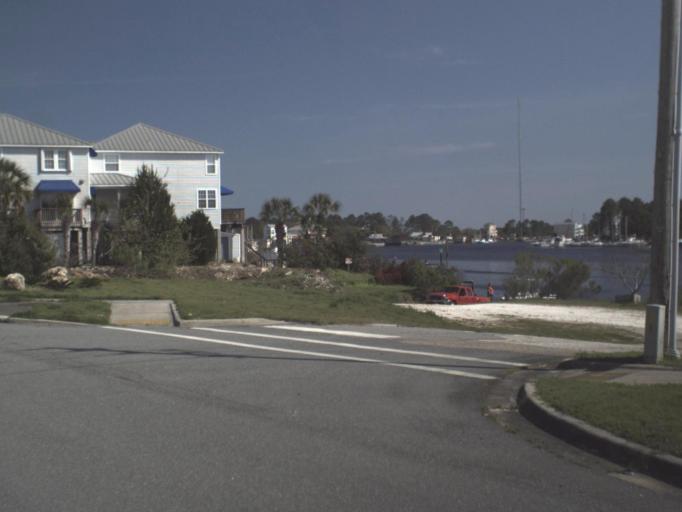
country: US
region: Florida
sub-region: Franklin County
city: Carrabelle
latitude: 29.8528
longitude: -84.6686
